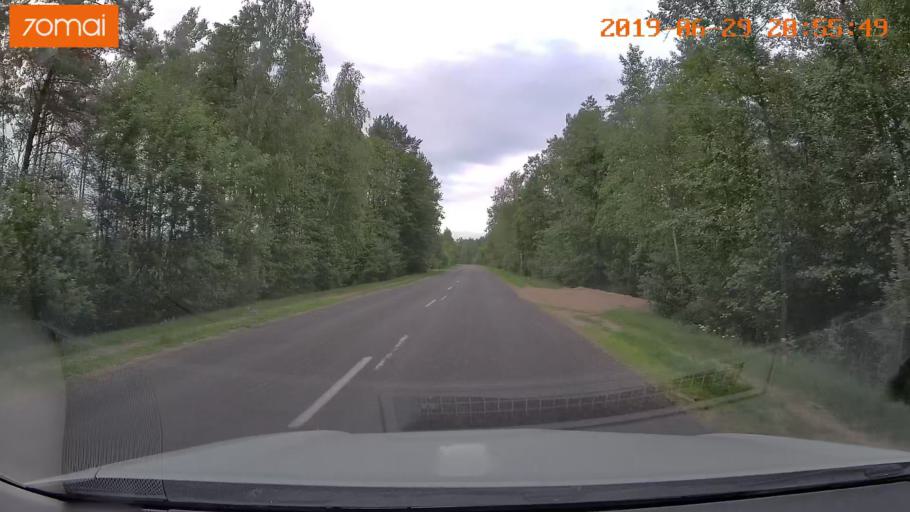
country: BY
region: Brest
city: Hantsavichy
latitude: 52.7039
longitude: 26.3668
